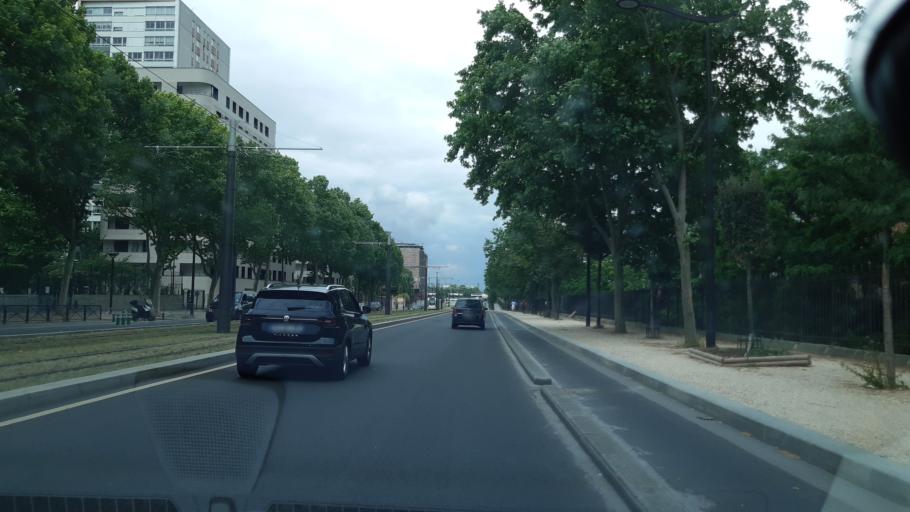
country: FR
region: Ile-de-France
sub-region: Paris
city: Saint-Ouen
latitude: 48.8981
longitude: 2.3473
